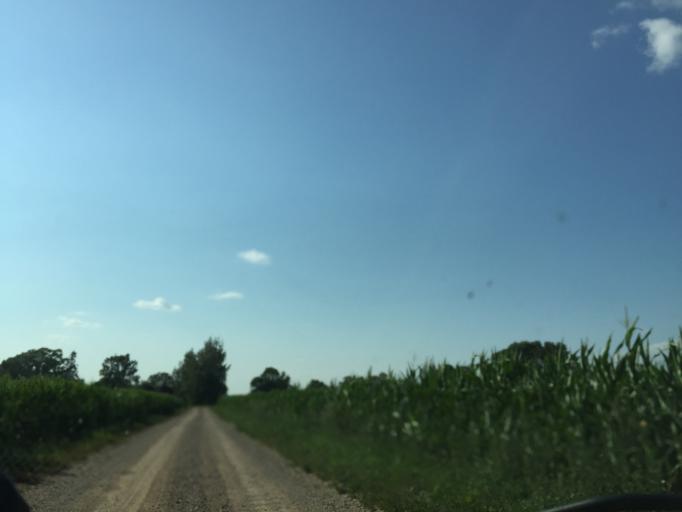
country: LV
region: Jelgava
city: Jelgava
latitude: 56.4670
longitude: 23.6768
